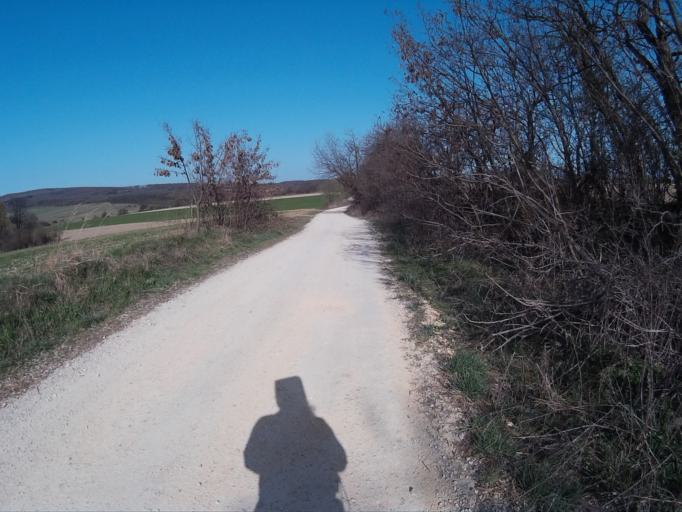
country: HU
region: Veszprem
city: Herend
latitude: 47.1981
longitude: 17.7902
